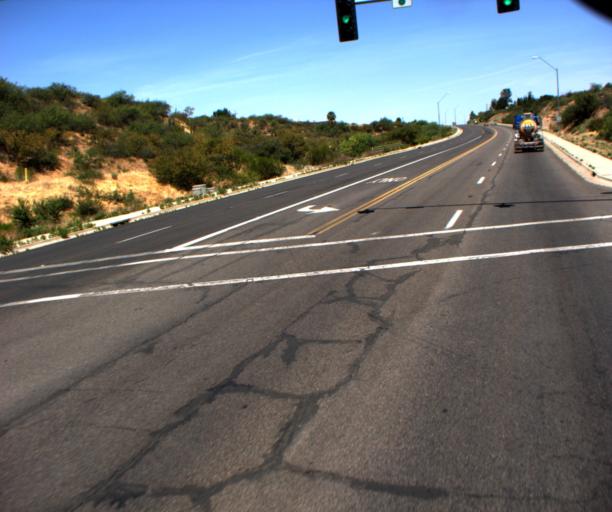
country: US
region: Arizona
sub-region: Gila County
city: Globe
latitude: 33.3792
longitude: -110.7482
